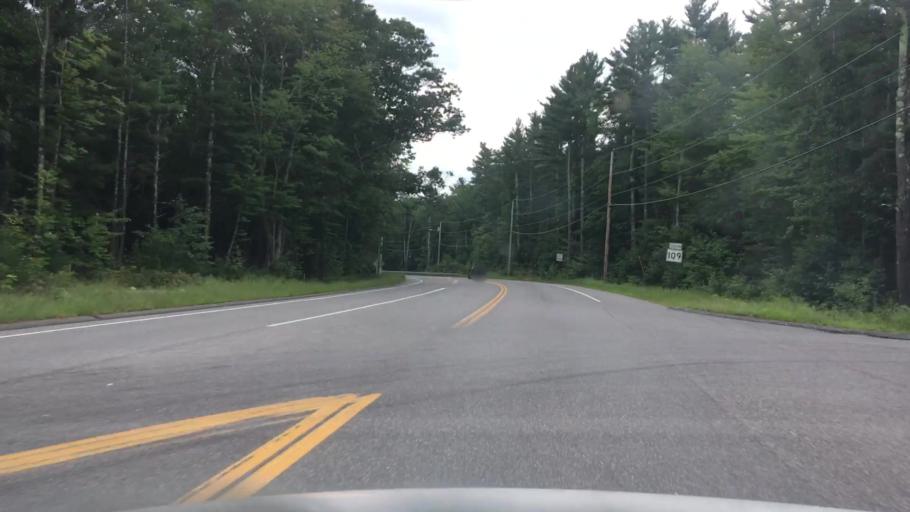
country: US
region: Maine
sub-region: York County
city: Wells Beach Station
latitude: 43.3464
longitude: -70.6448
